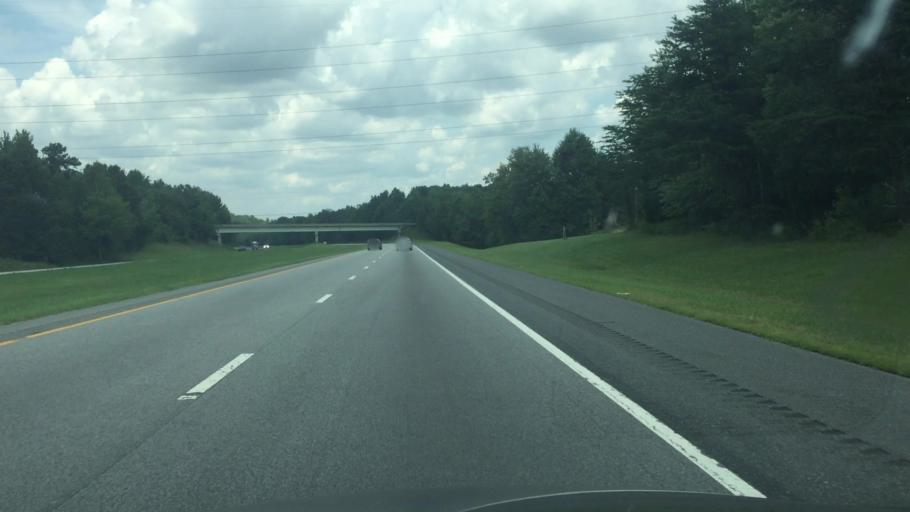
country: US
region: North Carolina
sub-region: Guilford County
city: Pleasant Garden
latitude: 35.9500
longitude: -79.8218
